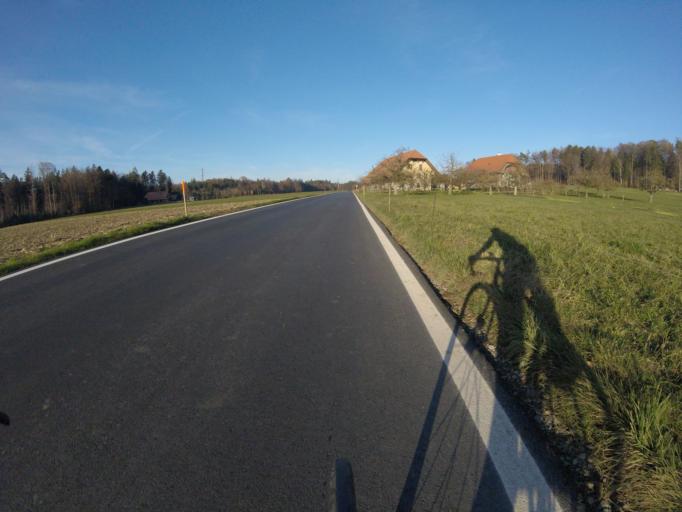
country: CH
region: Bern
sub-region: Bern-Mittelland District
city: Muhleberg
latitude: 46.9435
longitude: 7.2855
